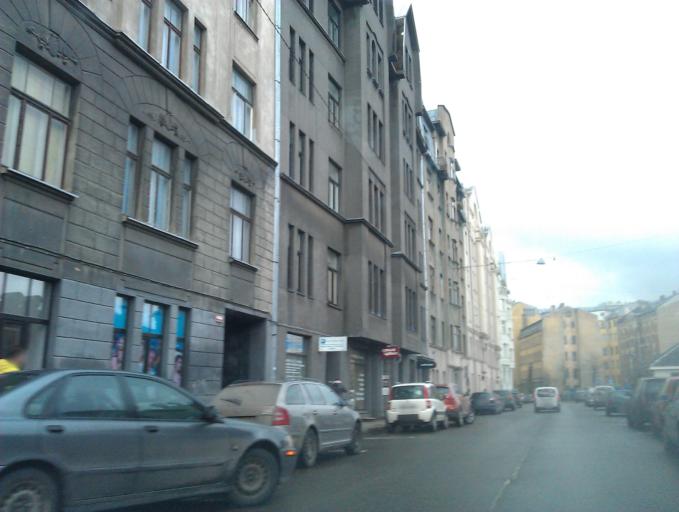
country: LV
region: Riga
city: Riga
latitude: 56.9606
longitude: 24.1149
